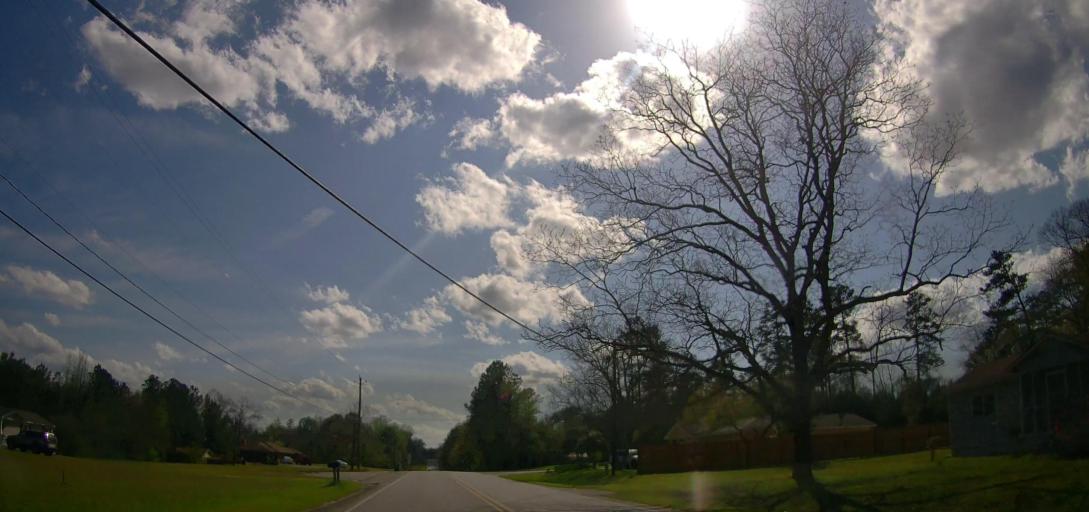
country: US
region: Georgia
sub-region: Wilkinson County
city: Gordon
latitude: 32.9735
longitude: -83.2824
